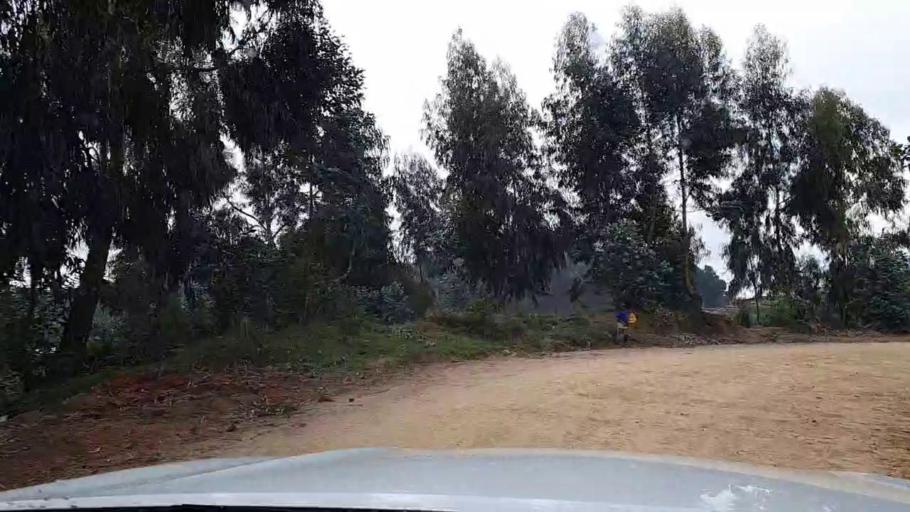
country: RW
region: Southern Province
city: Nzega
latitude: -2.3713
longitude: 29.3812
